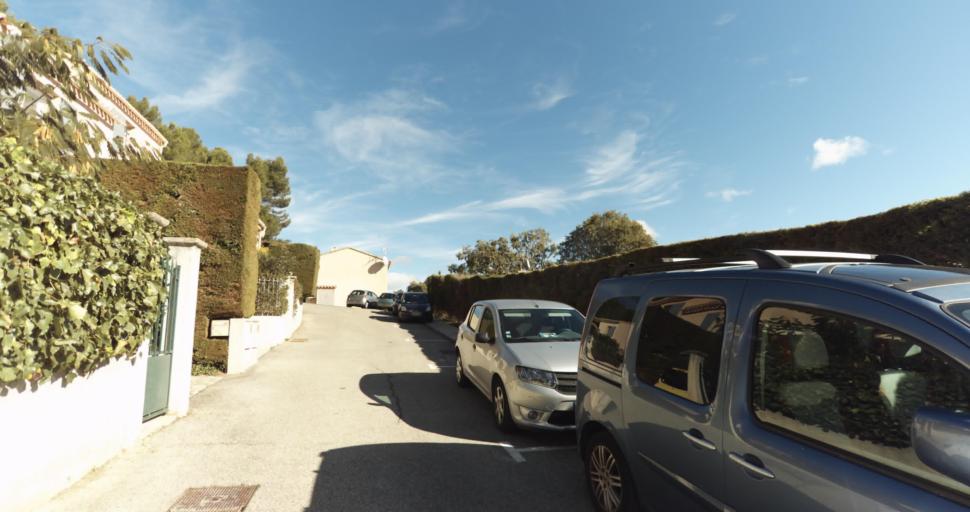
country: FR
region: Provence-Alpes-Cote d'Azur
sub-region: Departement des Bouches-du-Rhone
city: Venelles
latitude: 43.6010
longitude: 5.4763
